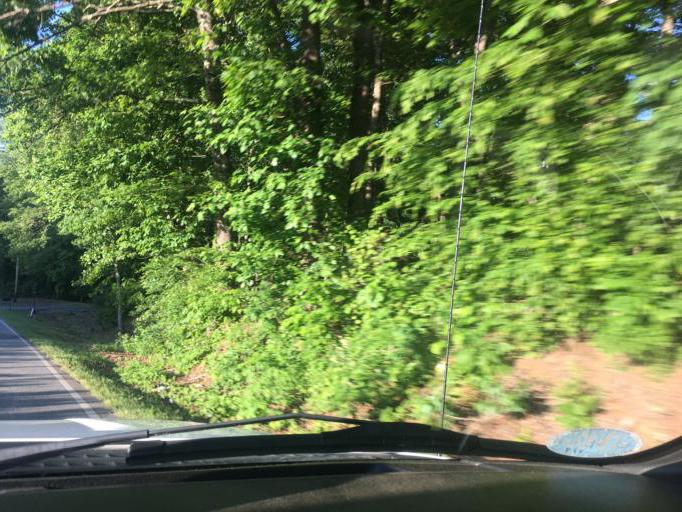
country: US
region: Georgia
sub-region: Forsyth County
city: Cumming
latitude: 34.2670
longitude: -84.1485
